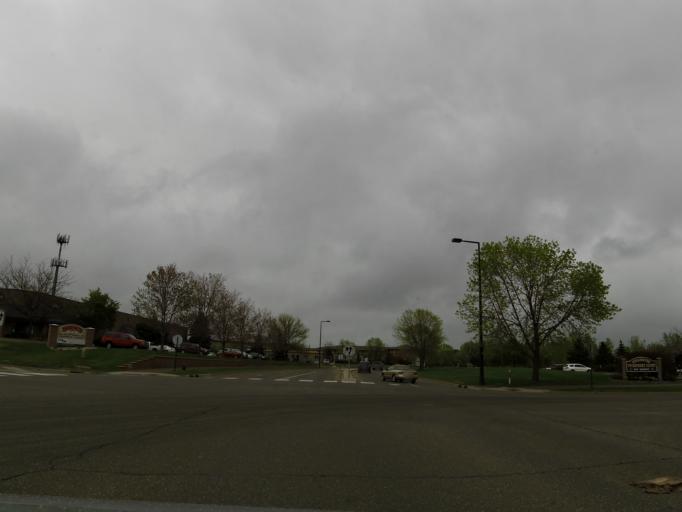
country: US
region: Minnesota
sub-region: Washington County
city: Stillwater
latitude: 45.0400
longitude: -92.8342
